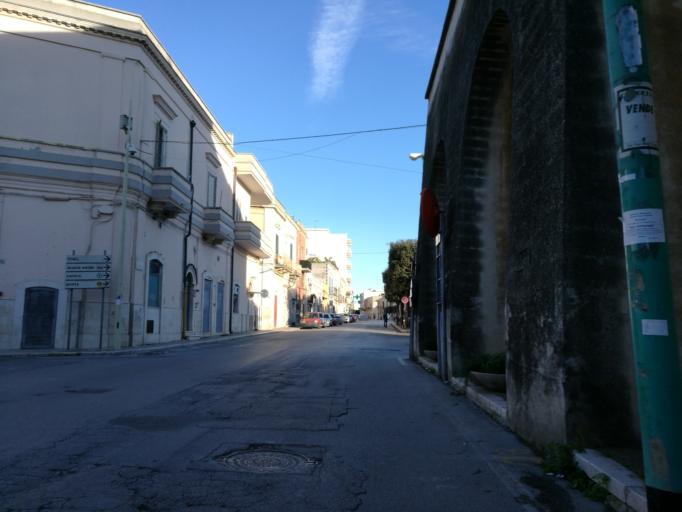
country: IT
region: Apulia
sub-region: Provincia di Bari
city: Adelfia
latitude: 41.0044
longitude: 16.8643
